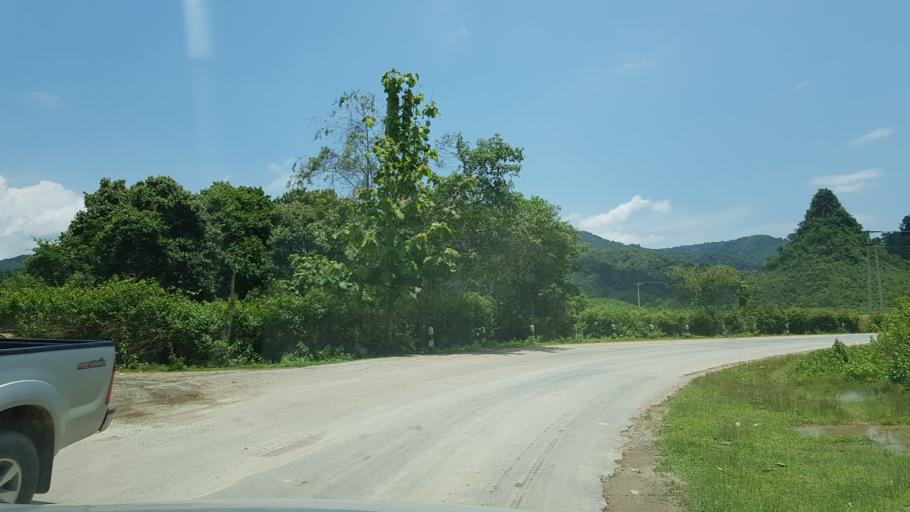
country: LA
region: Vientiane
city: Muang Kasi
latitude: 19.2752
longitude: 102.2171
